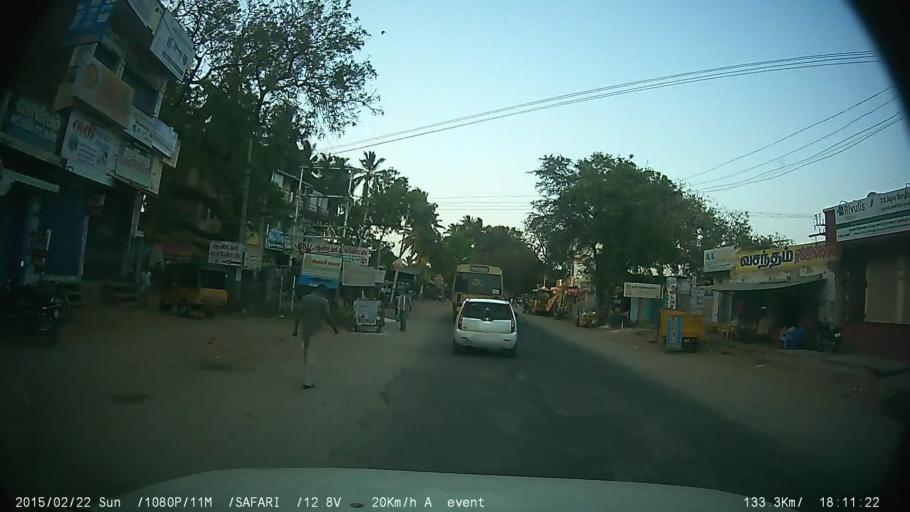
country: IN
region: Tamil Nadu
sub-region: Theni
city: Chinnamanur
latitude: 9.8436
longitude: 77.3803
